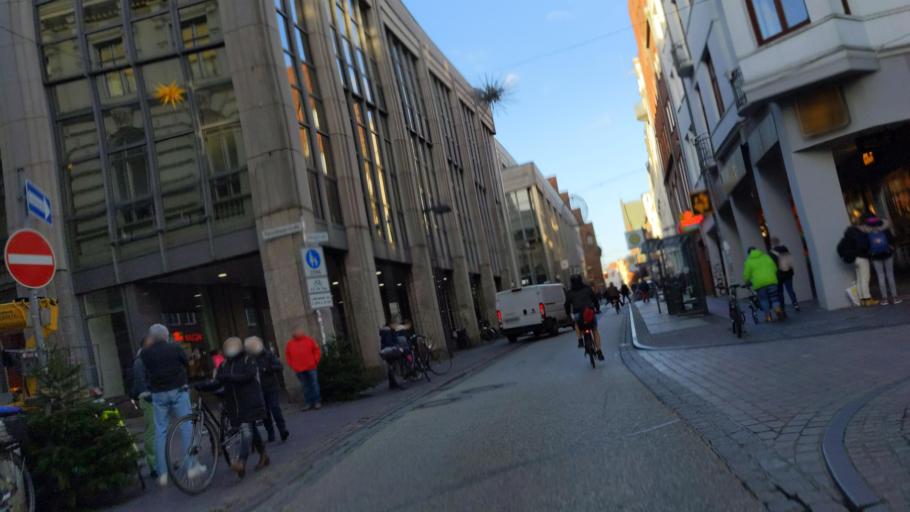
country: DE
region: Schleswig-Holstein
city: Luebeck
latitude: 53.8670
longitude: 10.6875
